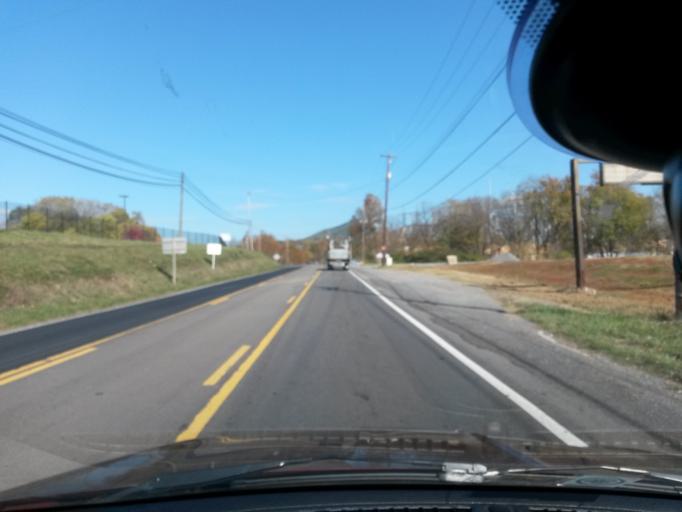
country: US
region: Virginia
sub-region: Botetourt County
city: Cloverdale
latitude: 37.3711
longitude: -79.9067
